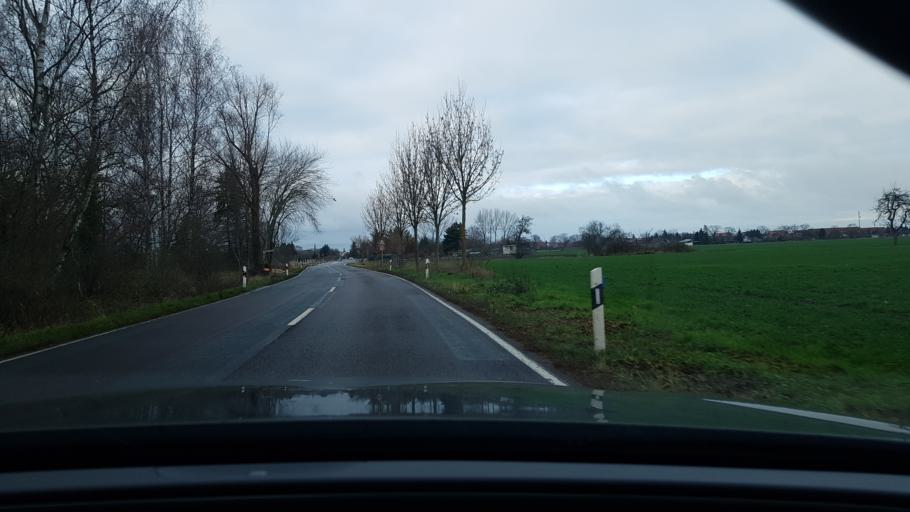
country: DE
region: Saxony-Anhalt
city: Oebisfelde
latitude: 52.4226
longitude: 11.0036
